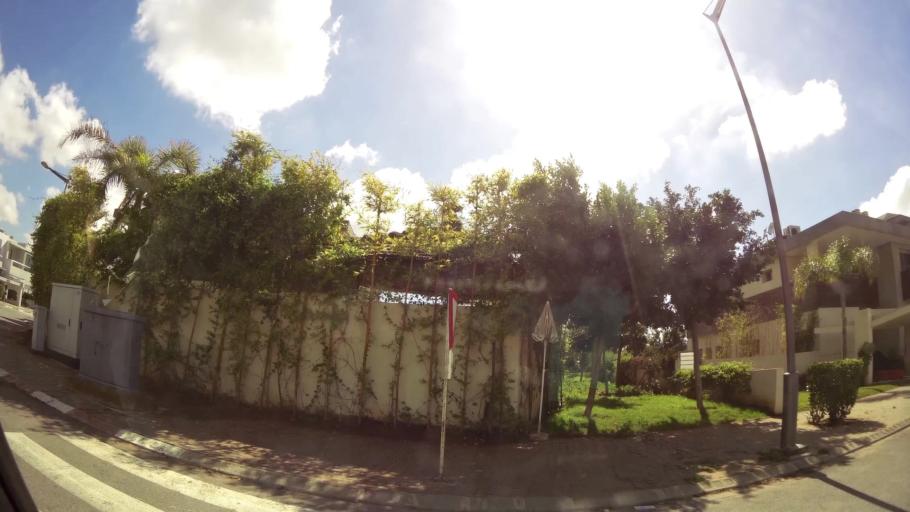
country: MA
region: Grand Casablanca
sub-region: Nouaceur
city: Bouskoura
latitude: 33.4678
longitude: -7.6031
